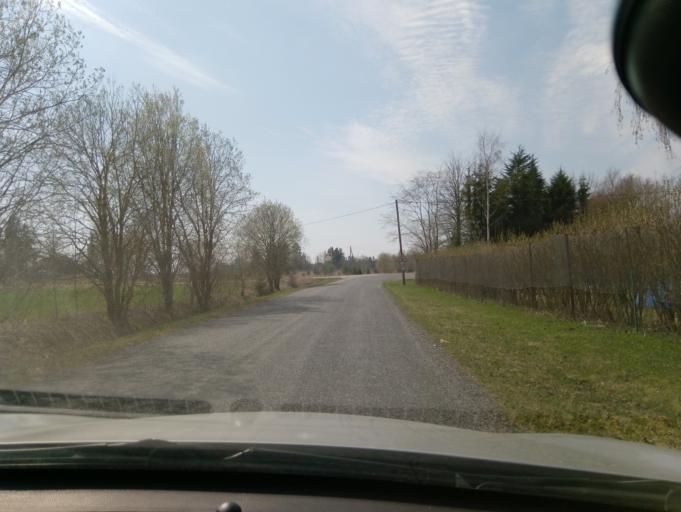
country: EE
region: Viljandimaa
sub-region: Vohma linn
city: Vohma
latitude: 58.6648
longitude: 25.5457
